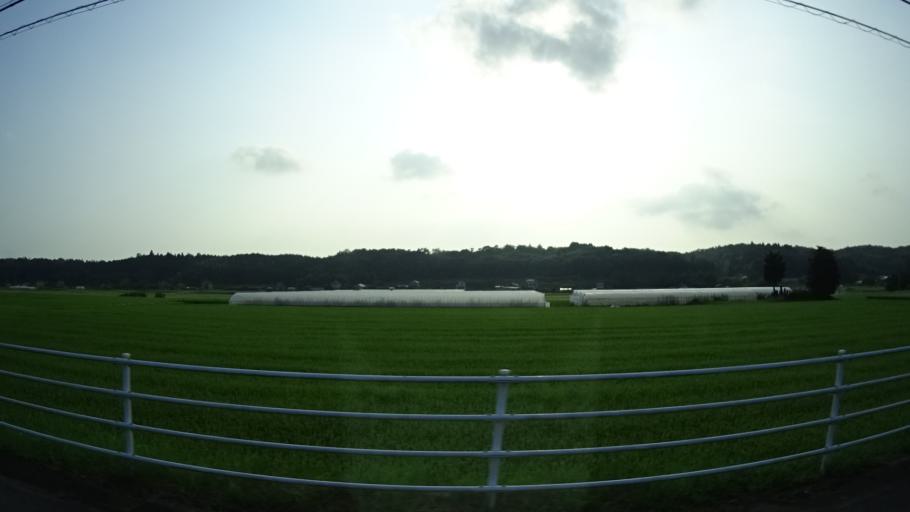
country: JP
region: Tochigi
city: Mashiko
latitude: 36.5524
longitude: 140.1024
